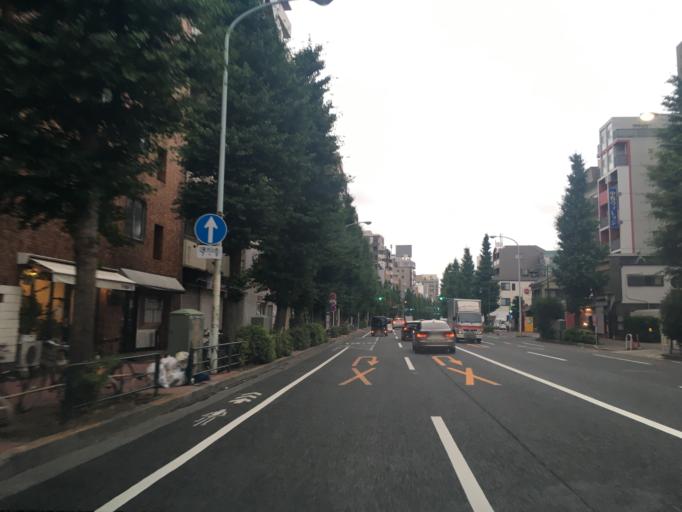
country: JP
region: Tokyo
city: Tokyo
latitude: 35.6975
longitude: 139.6637
